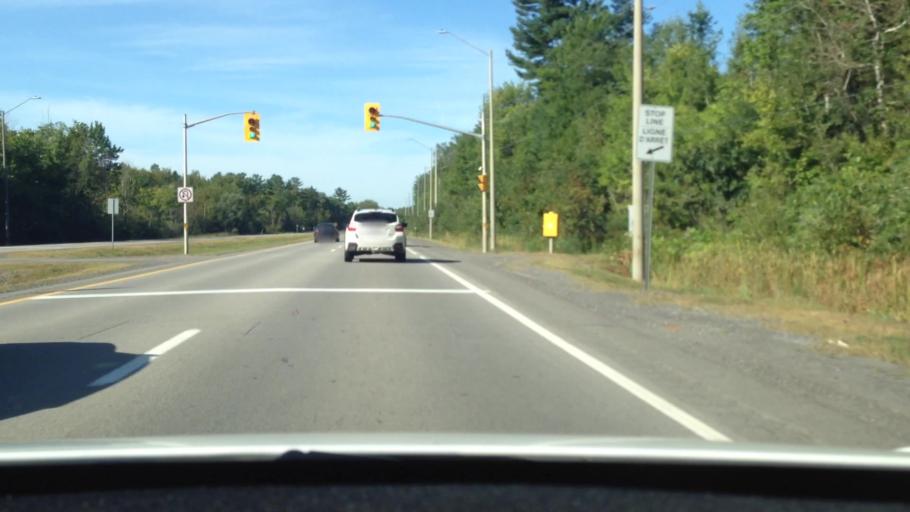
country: CA
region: Ontario
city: Ottawa
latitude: 45.4278
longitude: -75.5623
